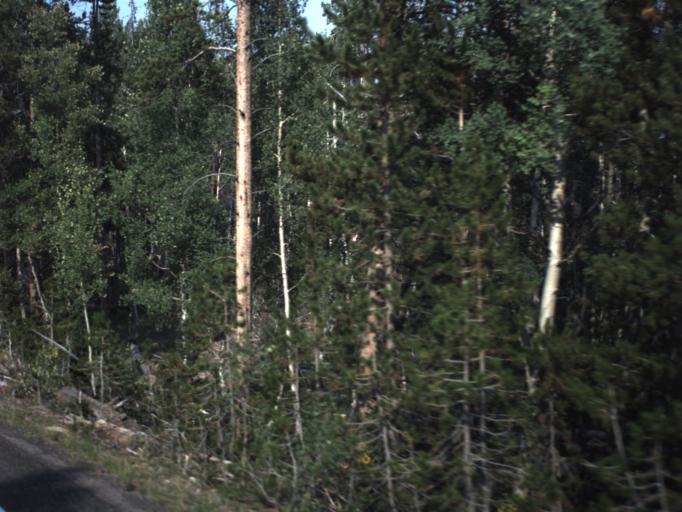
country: US
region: Utah
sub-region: Summit County
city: Oakley
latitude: 40.8154
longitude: -110.8720
